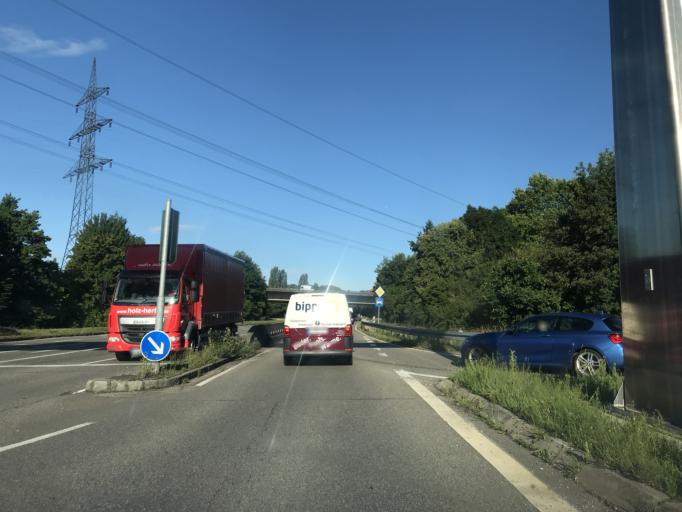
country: DE
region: Baden-Wuerttemberg
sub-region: Freiburg Region
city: Loerrach
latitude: 47.6325
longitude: 7.6757
